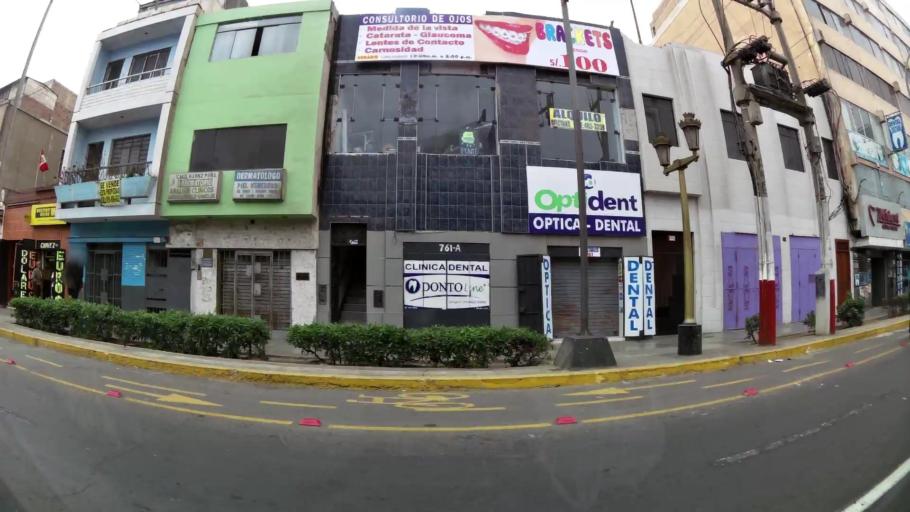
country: PE
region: Callao
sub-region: Callao
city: Callao
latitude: -12.0600
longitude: -77.1376
